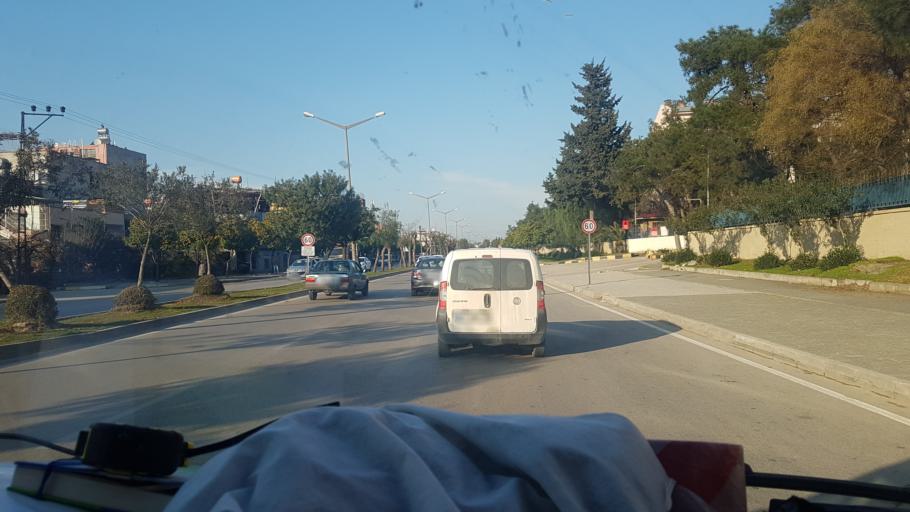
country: TR
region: Adana
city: Adana
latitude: 37.0153
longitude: 35.3395
